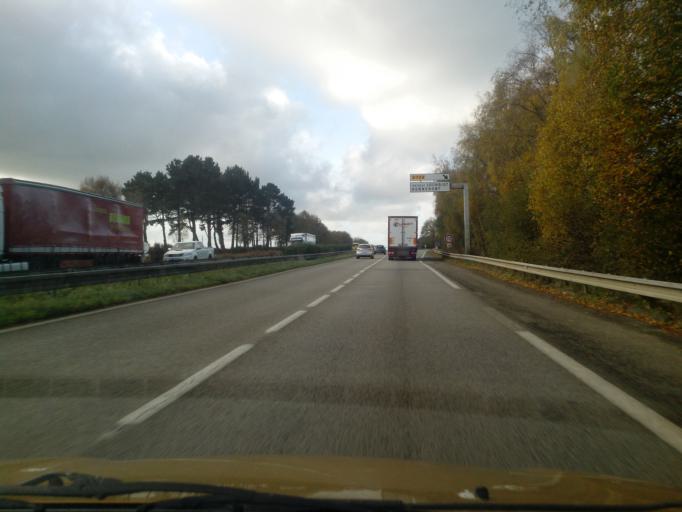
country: FR
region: Brittany
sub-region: Departement du Morbihan
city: Branderion
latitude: 47.8188
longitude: -3.2163
